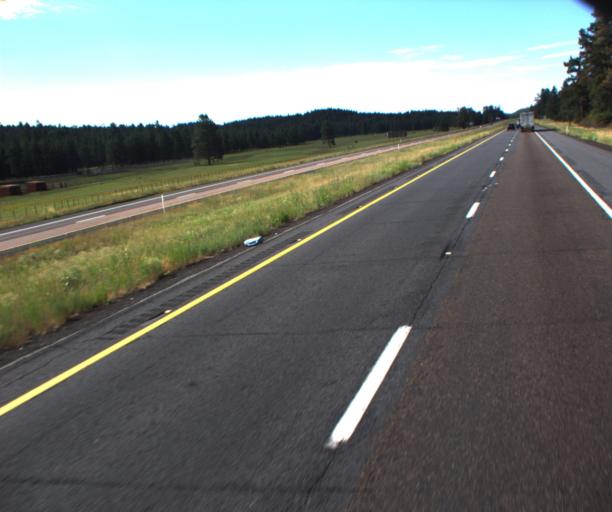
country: US
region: Arizona
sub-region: Coconino County
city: Mountainaire
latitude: 35.0110
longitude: -111.6854
